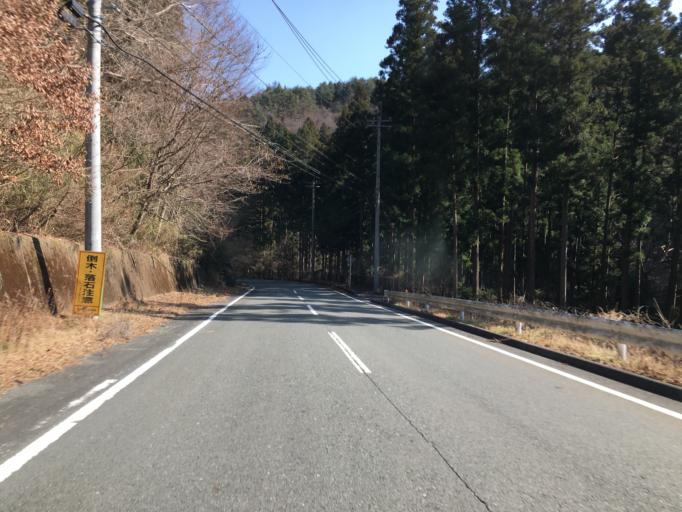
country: JP
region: Ibaraki
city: Takahagi
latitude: 36.8033
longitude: 140.6158
